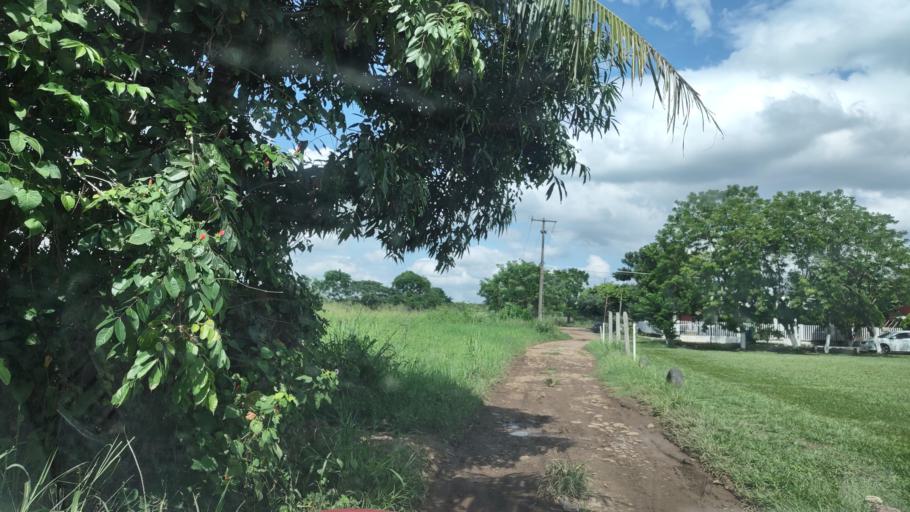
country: MX
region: Veracruz
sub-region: Martinez de la Torre
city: La Union Paso Largo
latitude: 20.1286
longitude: -96.9985
